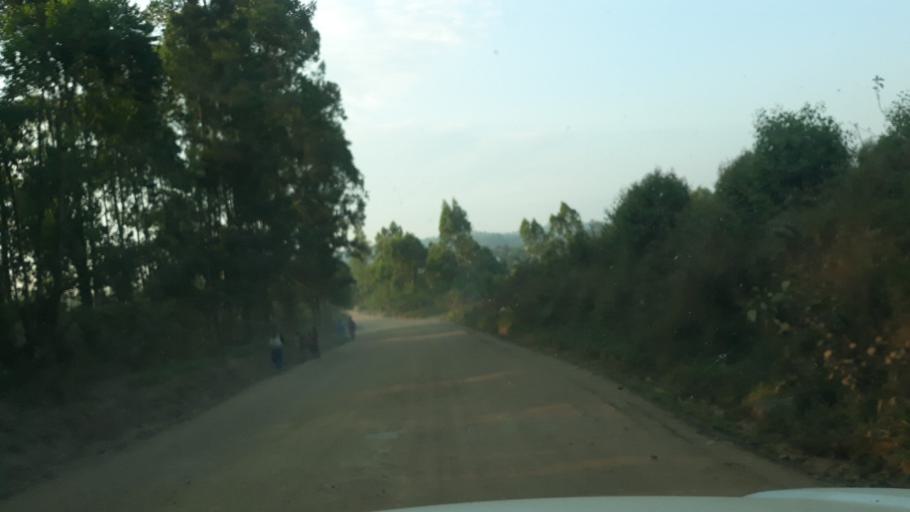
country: CD
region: South Kivu
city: Bukavu
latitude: -2.6684
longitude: 28.8757
